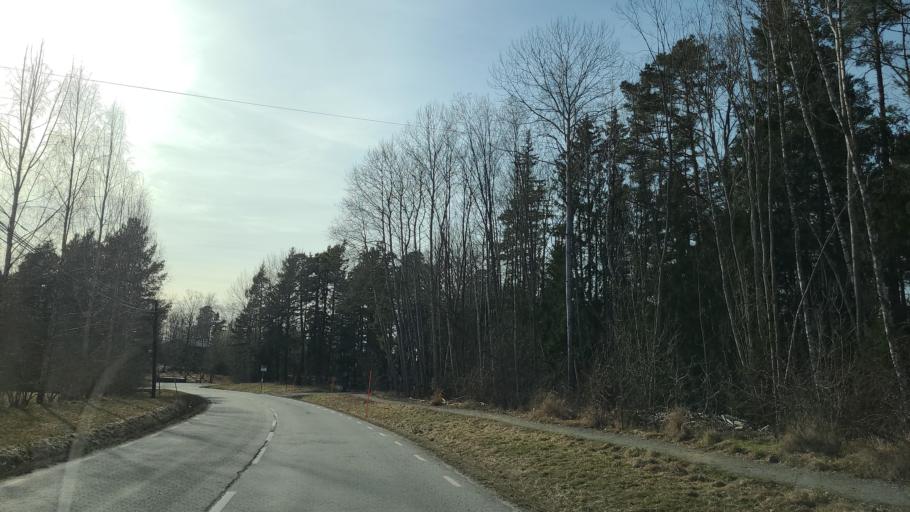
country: SE
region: Stockholm
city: Stenhamra
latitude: 59.2772
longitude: 17.6863
